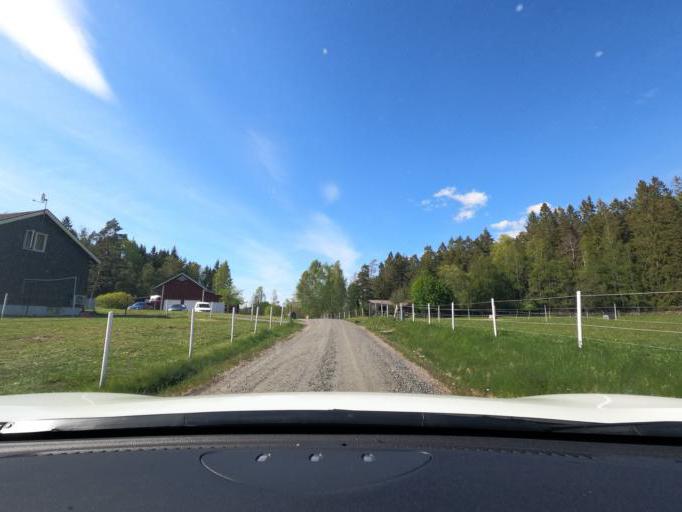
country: SE
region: Vaestra Goetaland
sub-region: Harryda Kommun
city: Ravlanda
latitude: 57.5909
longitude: 12.4878
